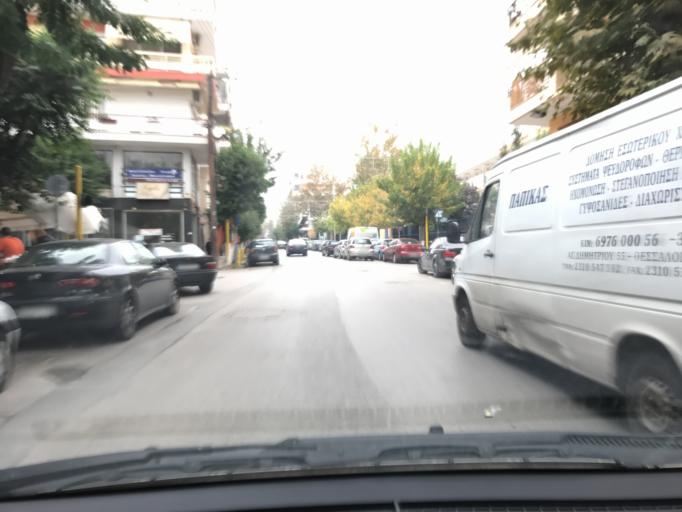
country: GR
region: Central Macedonia
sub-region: Nomos Thessalonikis
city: Ampelokipoi
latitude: 40.6530
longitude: 22.9257
